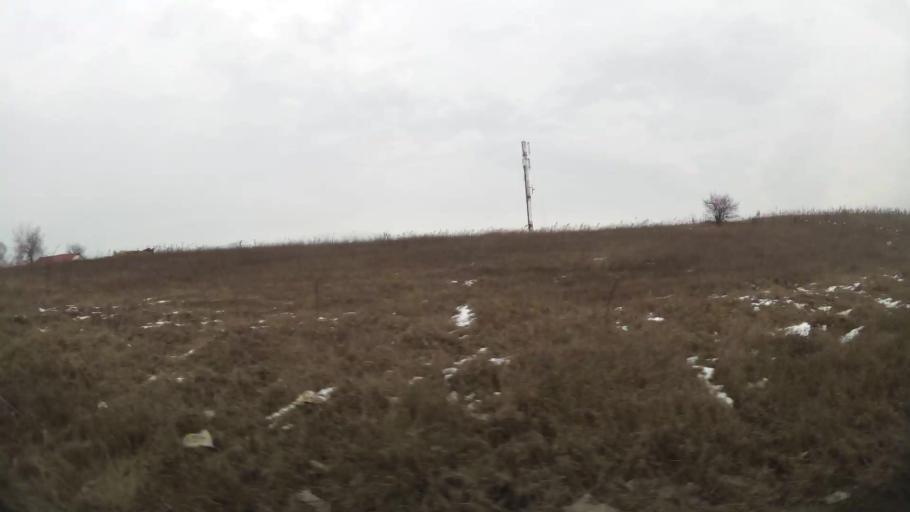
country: MK
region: Butel
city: Butel
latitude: 42.0410
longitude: 21.4388
